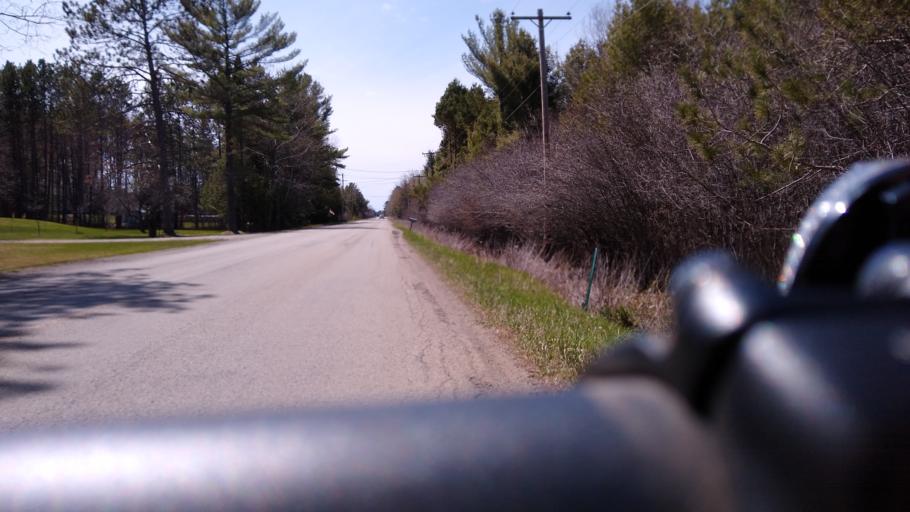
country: US
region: Michigan
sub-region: Delta County
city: Escanaba
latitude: 45.7353
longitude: -87.1701
